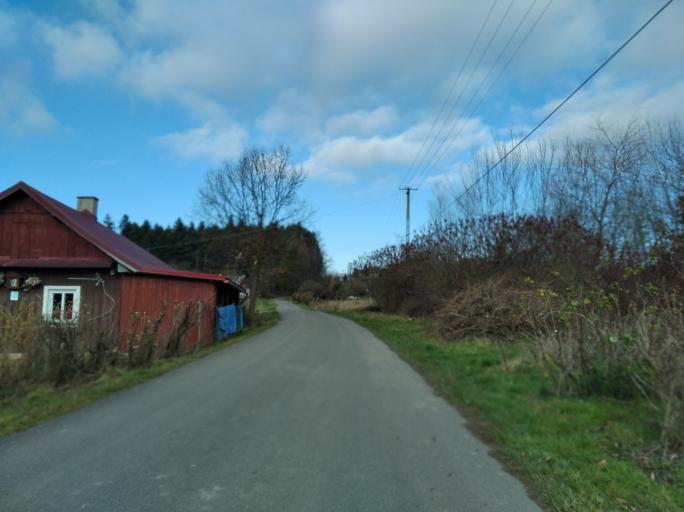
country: PL
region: Subcarpathian Voivodeship
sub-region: Powiat strzyzowski
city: Babica
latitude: 49.9065
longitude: 21.8501
